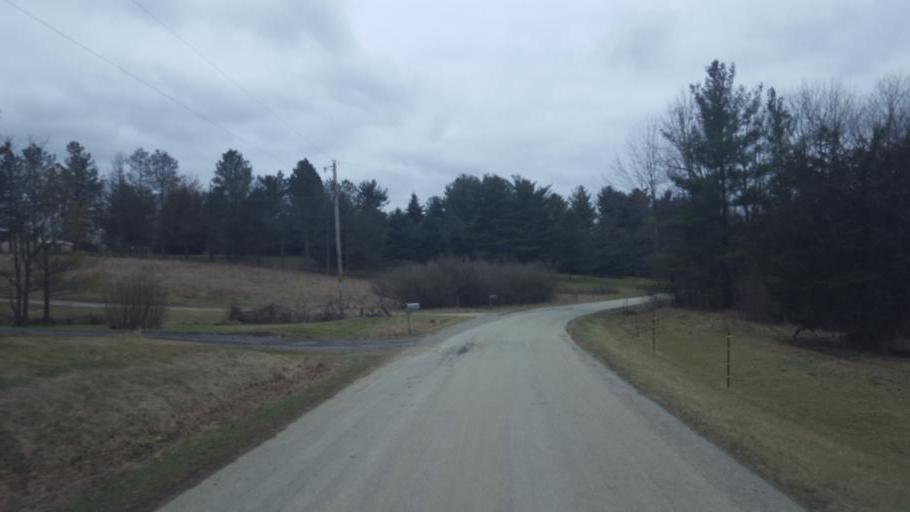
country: US
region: Ohio
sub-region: Morrow County
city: Mount Gilead
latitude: 40.5667
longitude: -82.7719
